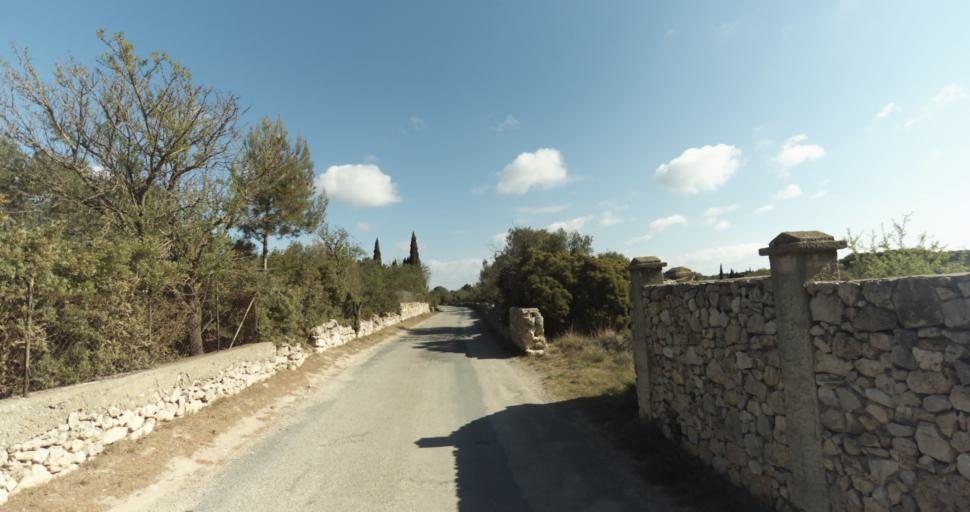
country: FR
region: Languedoc-Roussillon
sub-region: Departement de l'Aude
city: Leucate
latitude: 42.9146
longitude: 3.0309
